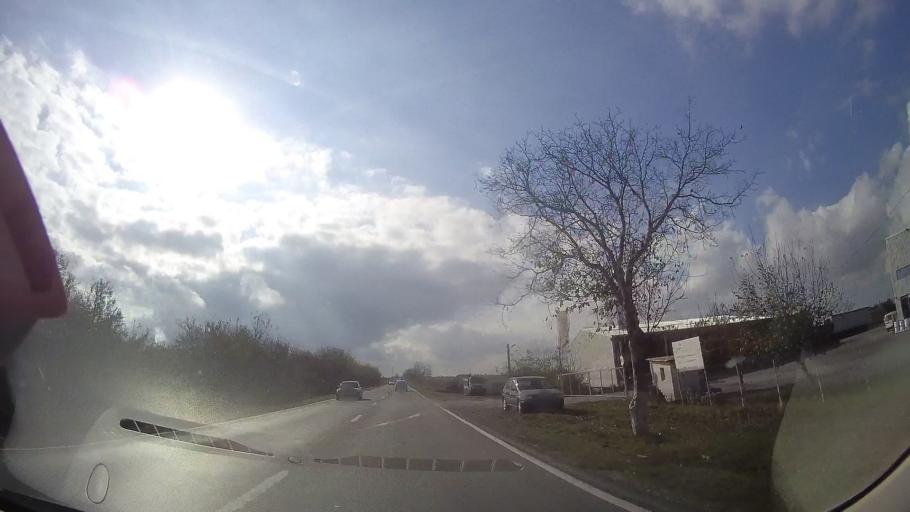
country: RO
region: Constanta
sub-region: Comuna Agigea
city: Agigea
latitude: 44.0821
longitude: 28.6049
